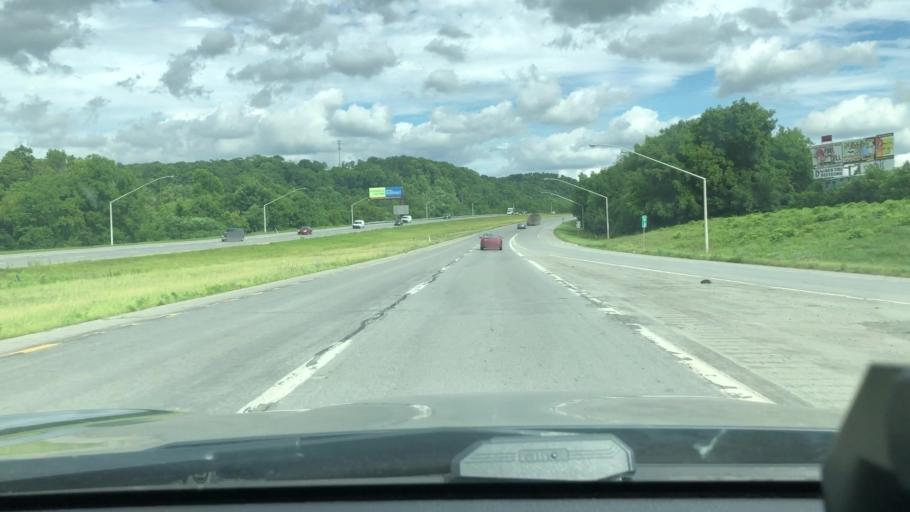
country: US
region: Pennsylvania
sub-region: Northampton County
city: Tatamy
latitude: 40.7574
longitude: -75.2704
